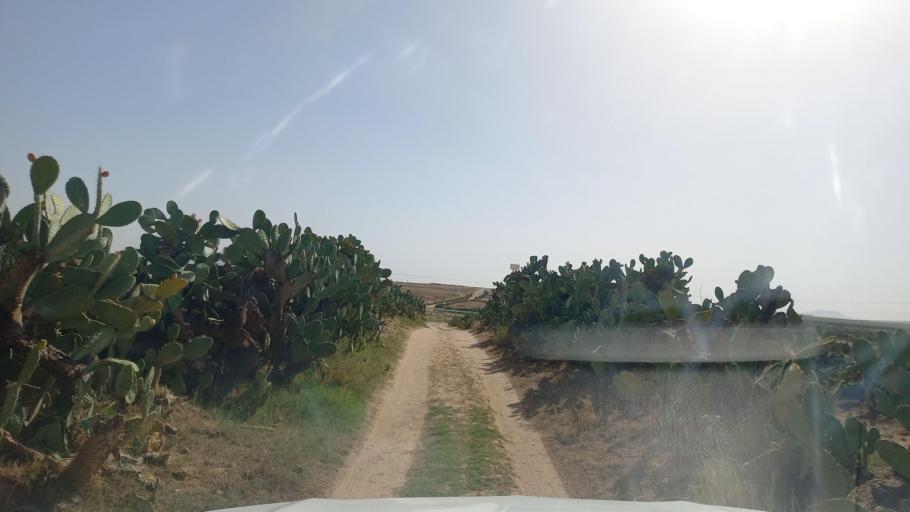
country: TN
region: Al Qasrayn
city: Sbiba
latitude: 35.3164
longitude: 9.0238
